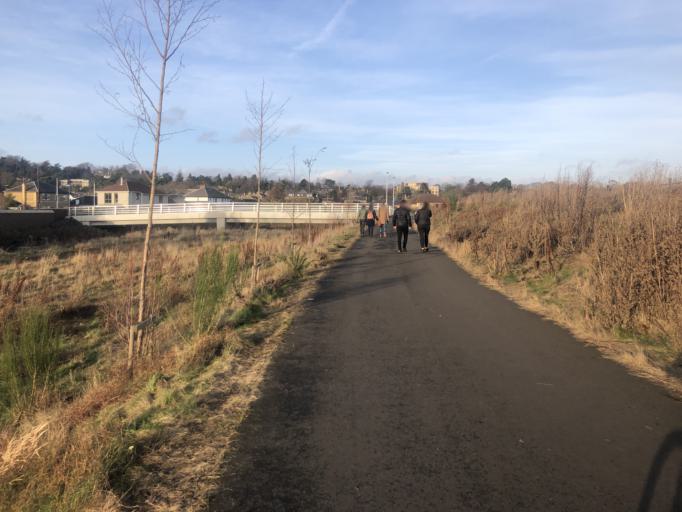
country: GB
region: Scotland
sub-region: Edinburgh
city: Colinton
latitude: 55.9413
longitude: -3.2464
